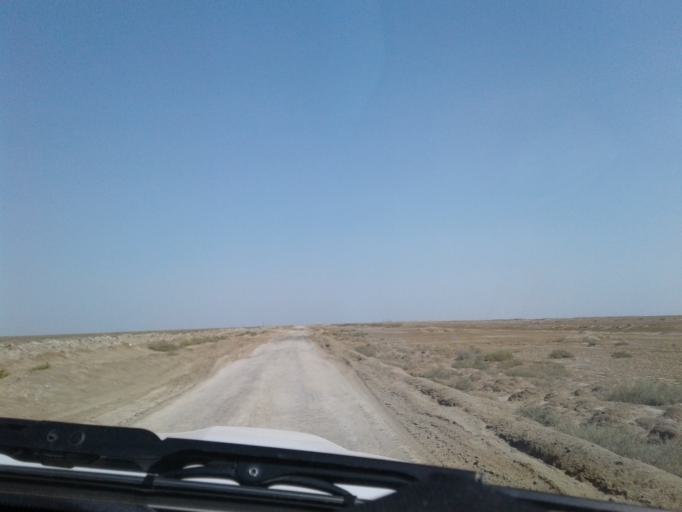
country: IR
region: Golestan
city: Gomishan
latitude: 37.8283
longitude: 53.9215
